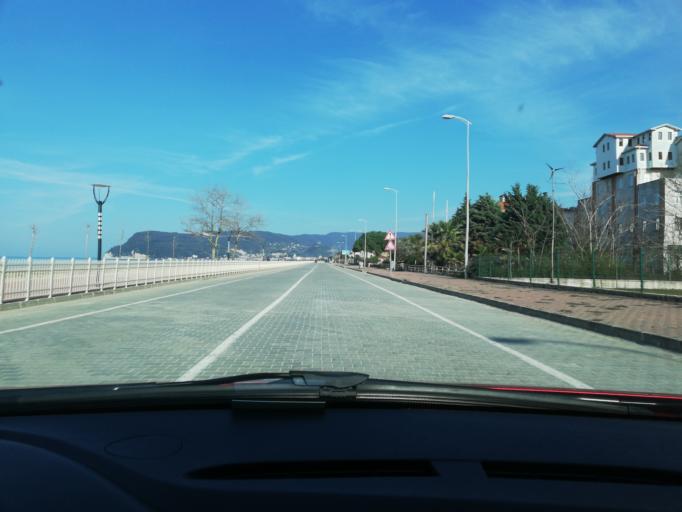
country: TR
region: Kastamonu
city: Cide
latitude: 41.8839
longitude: 32.9502
